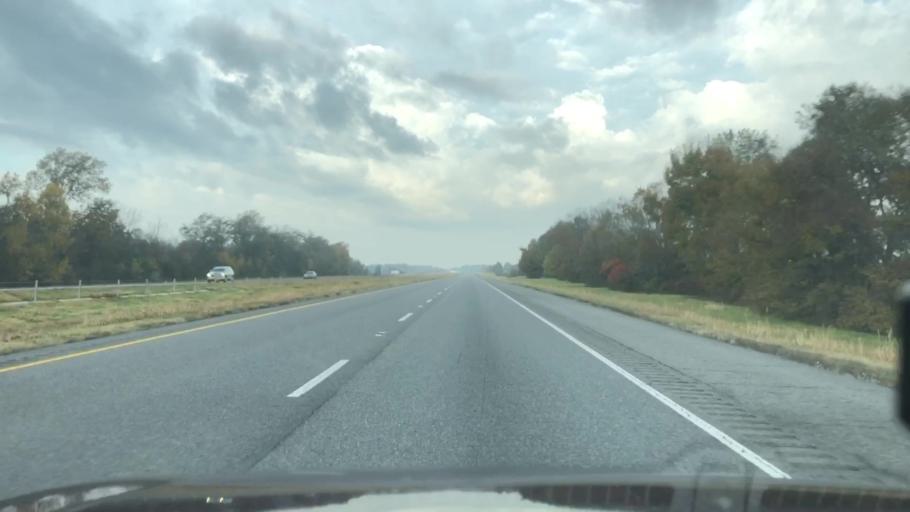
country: US
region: Louisiana
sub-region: Madison Parish
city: Tallulah
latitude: 32.4138
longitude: -91.2691
